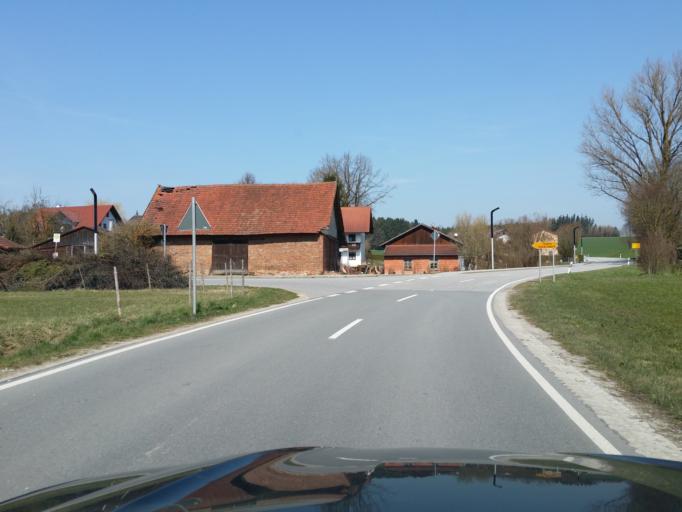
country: DE
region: Bavaria
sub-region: Upper Bavaria
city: Kirchberg
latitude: 48.4394
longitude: 12.0632
